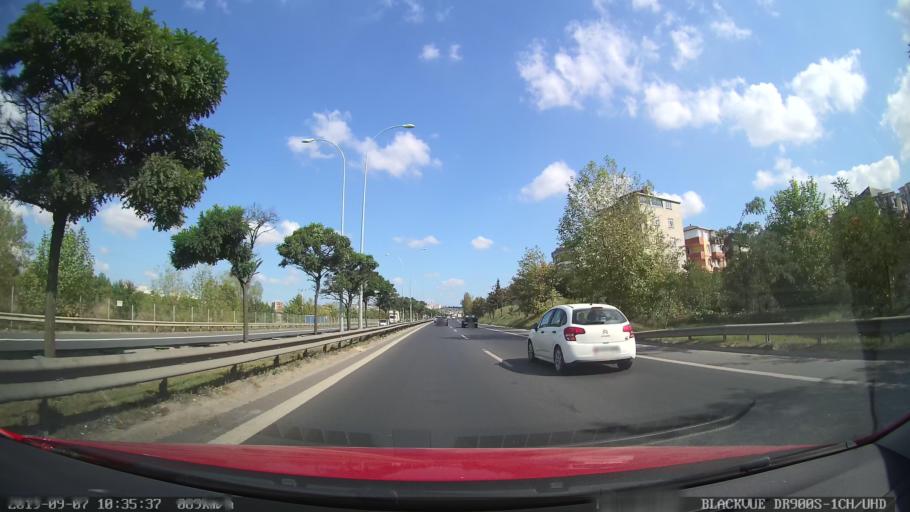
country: TR
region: Kocaeli
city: Darica
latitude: 40.8214
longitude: 29.3649
